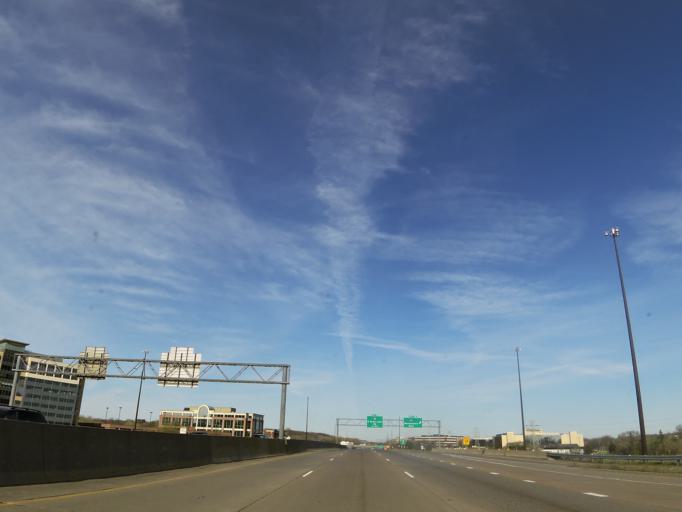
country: US
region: Minnesota
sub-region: Hennepin County
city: Edina
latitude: 44.8589
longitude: -93.3488
